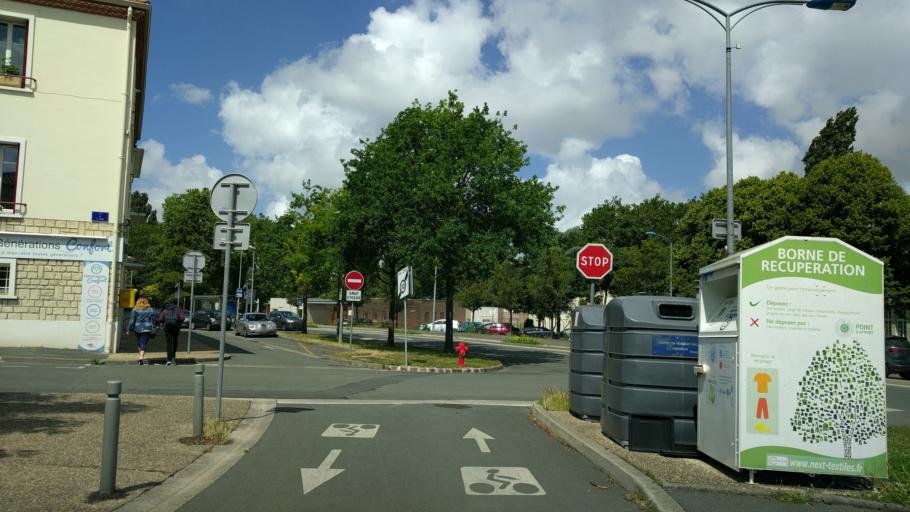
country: FR
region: Poitou-Charentes
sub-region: Departement de la Charente-Maritime
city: La Rochelle
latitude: 46.1694
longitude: -1.1478
